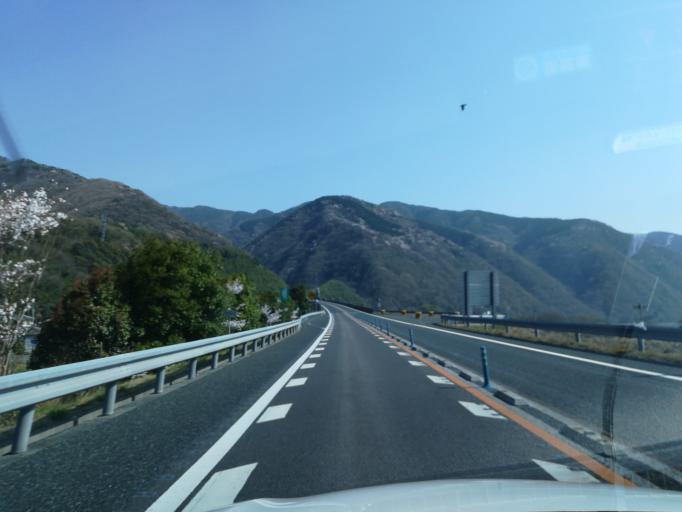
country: JP
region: Tokushima
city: Ikedacho
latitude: 34.0441
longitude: 133.9118
